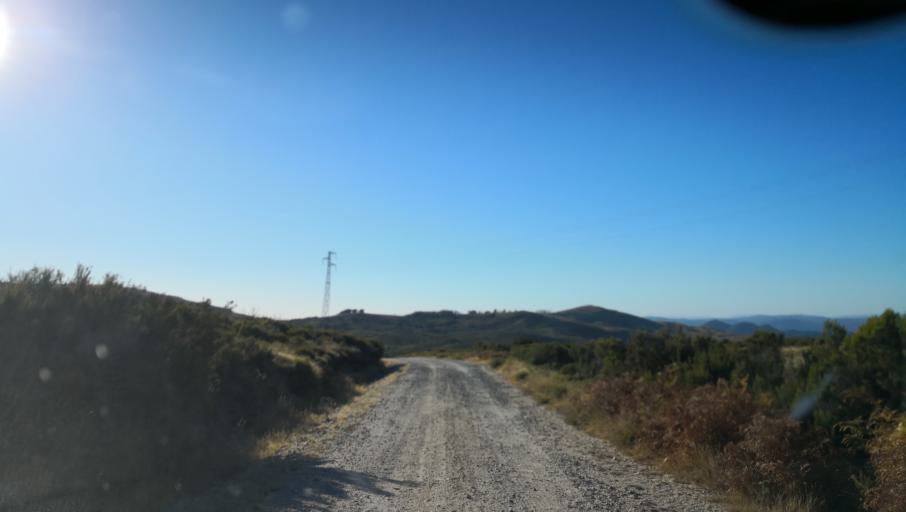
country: PT
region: Vila Real
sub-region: Vila Real
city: Vila Real
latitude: 41.3554
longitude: -7.7816
